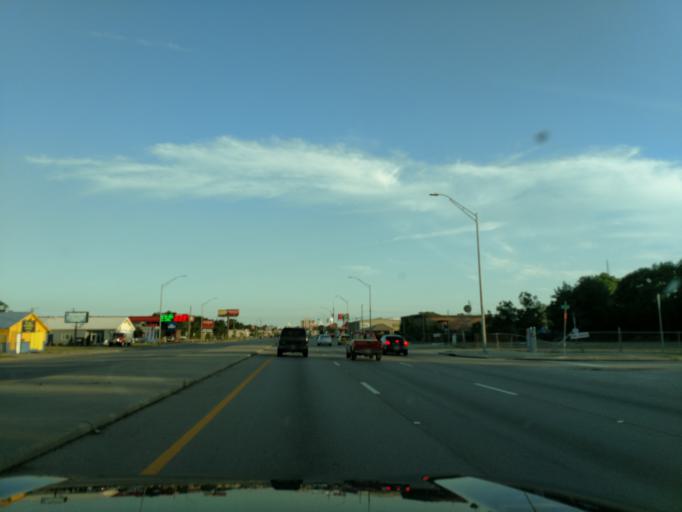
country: US
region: Mississippi
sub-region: Harrison County
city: West Gulfport
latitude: 30.3882
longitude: -89.0932
